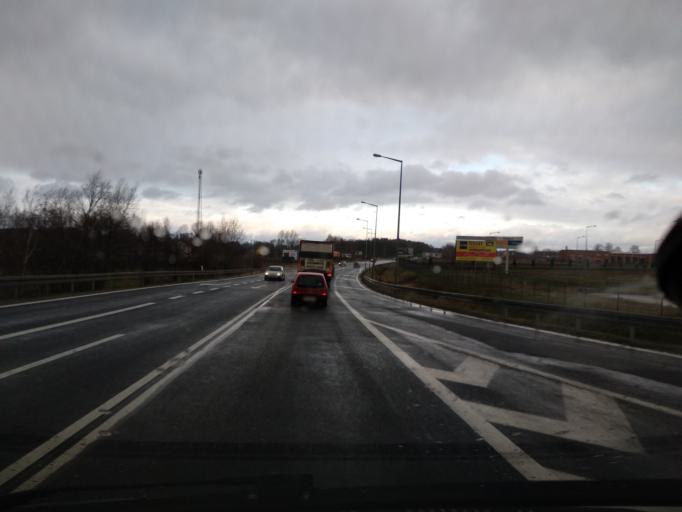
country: PL
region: Greater Poland Voivodeship
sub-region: Powiat koninski
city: Stare Miasto
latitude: 52.1654
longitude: 18.2077
